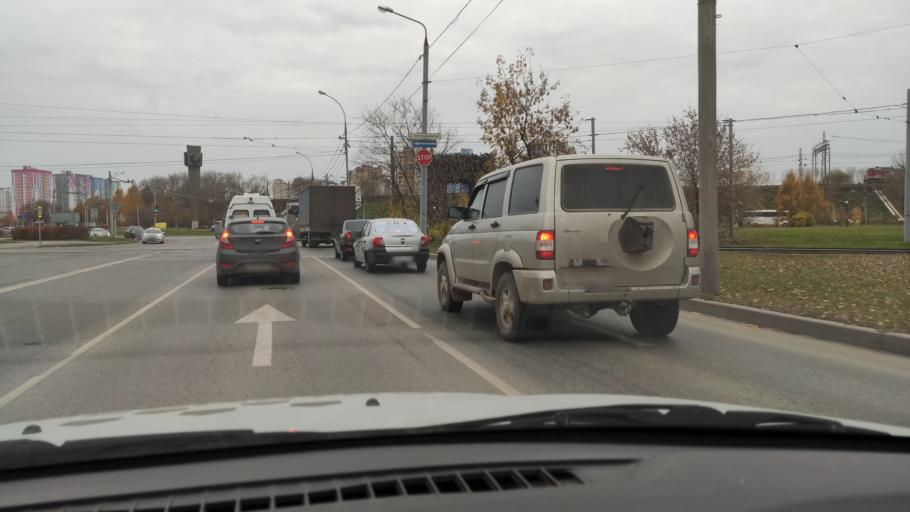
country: RU
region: Perm
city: Perm
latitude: 58.0056
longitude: 56.1935
